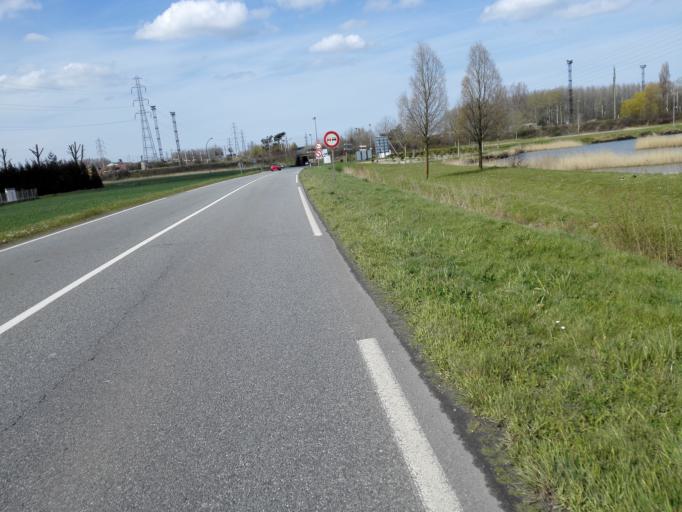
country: FR
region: Nord-Pas-de-Calais
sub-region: Departement du Nord
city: Grande-Synthe
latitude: 50.9948
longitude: 2.2945
